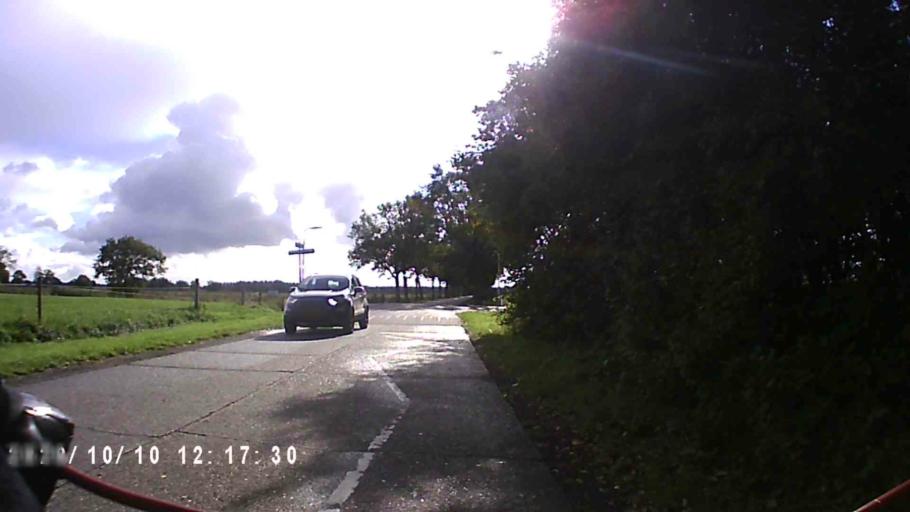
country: NL
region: Friesland
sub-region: Gemeente Heerenveen
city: Jubbega
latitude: 53.0193
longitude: 6.1706
